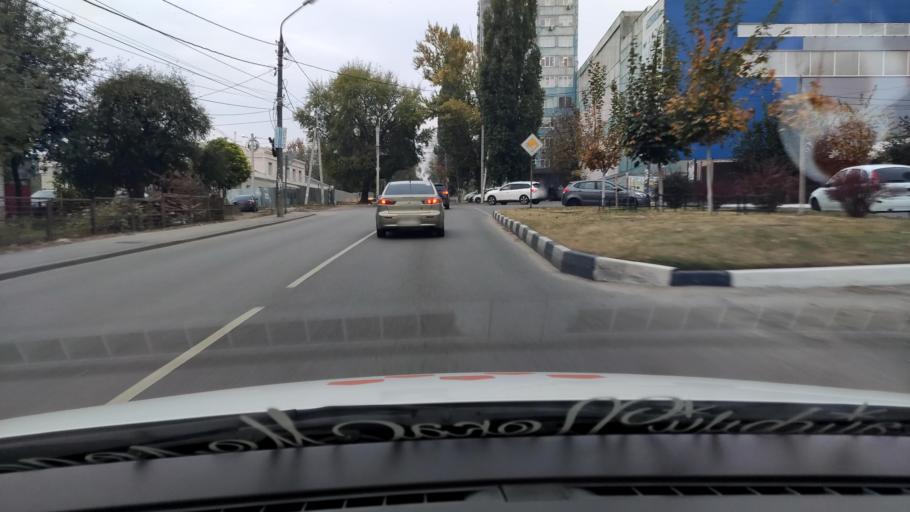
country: RU
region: Voronezj
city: Voronezh
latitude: 51.6916
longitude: 39.1903
